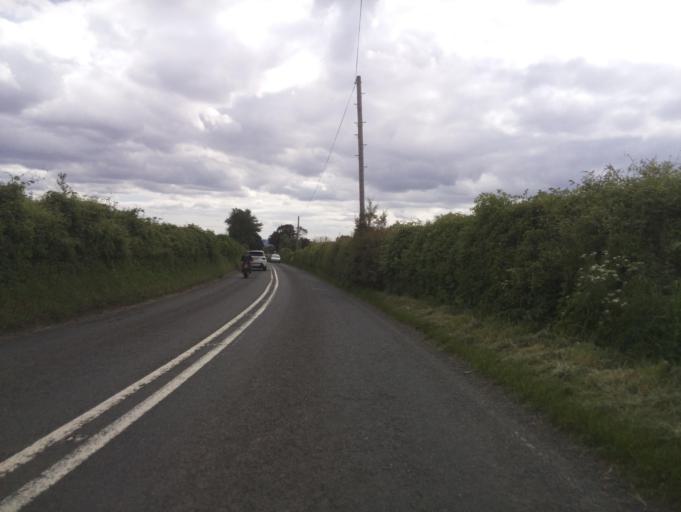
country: GB
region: England
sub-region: Herefordshire
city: Ross on Wye
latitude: 51.9417
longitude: -2.5542
